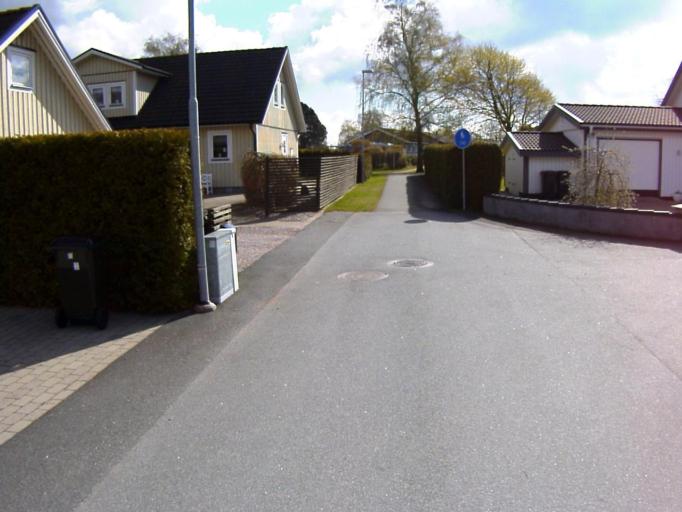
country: SE
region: Skane
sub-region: Kristianstads Kommun
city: Kristianstad
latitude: 56.0102
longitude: 14.0965
